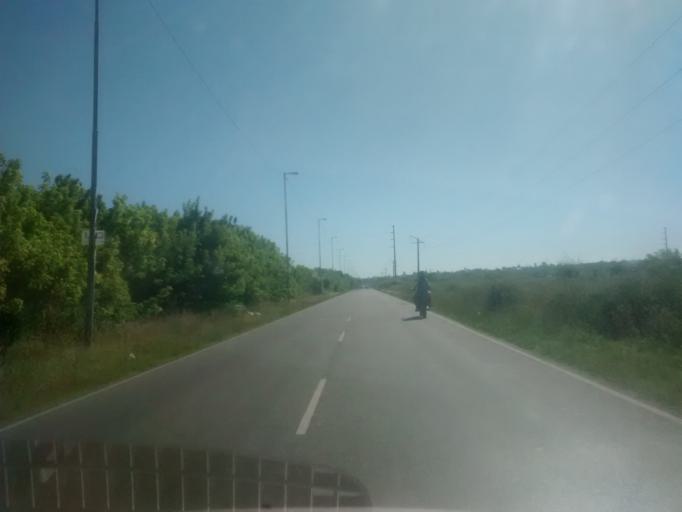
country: AR
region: Buenos Aires
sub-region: Partido de Berisso
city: Berisso
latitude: -34.9037
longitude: -57.9002
